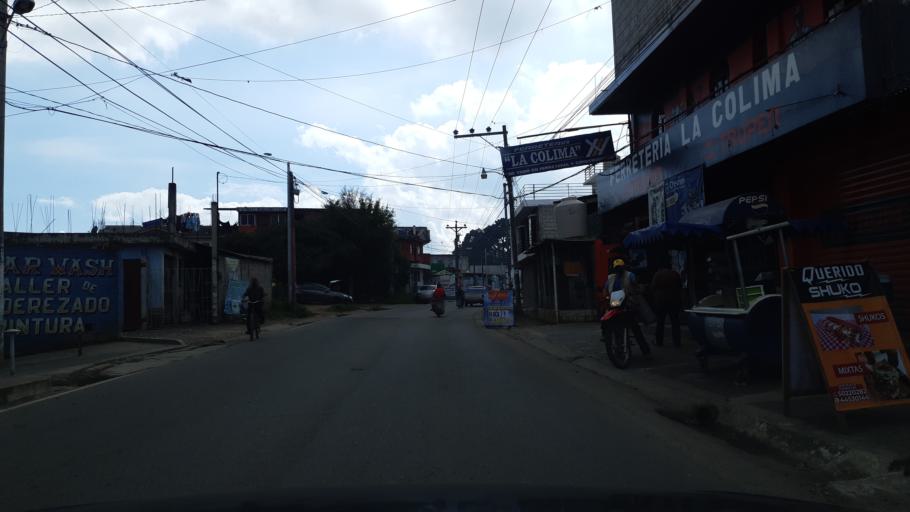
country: GT
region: Chimaltenango
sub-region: Municipio de Chimaltenango
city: Chimaltenango
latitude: 14.6704
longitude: -90.8068
